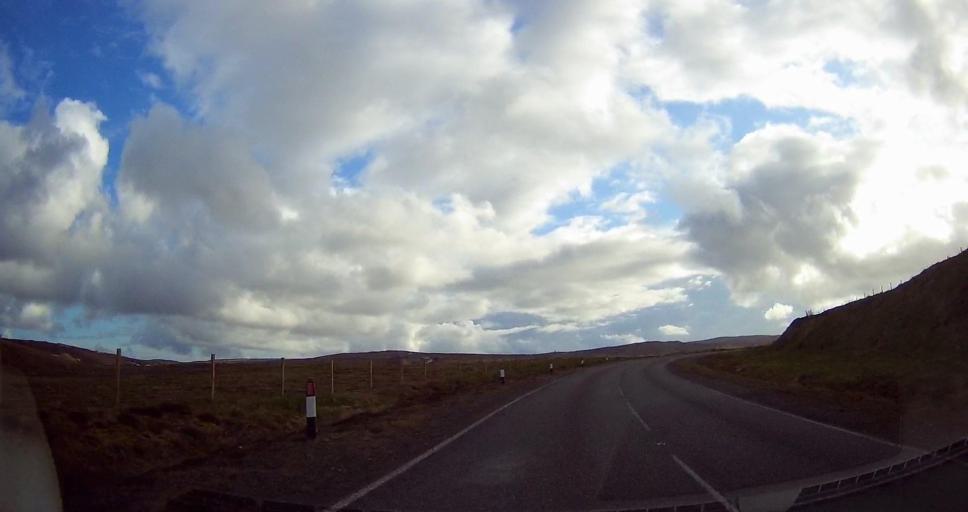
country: GB
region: Scotland
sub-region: Shetland Islands
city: Lerwick
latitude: 60.3504
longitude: -1.2070
